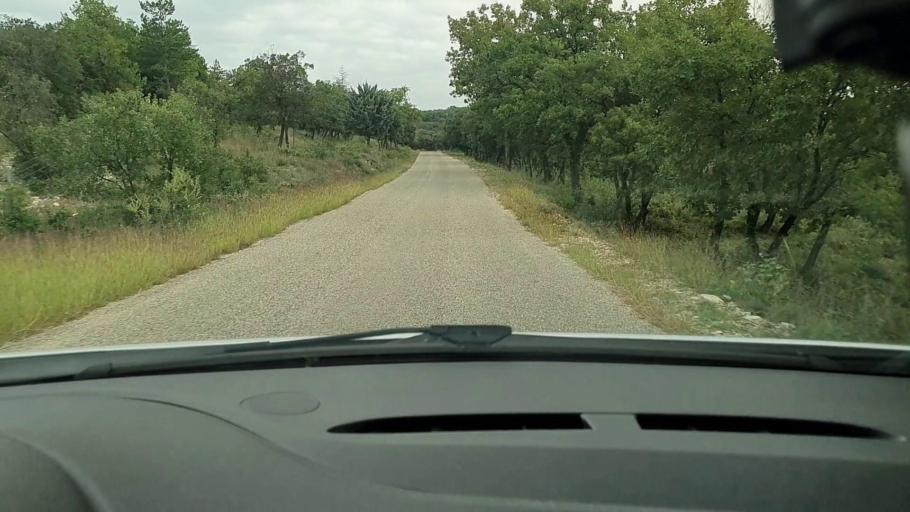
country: FR
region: Languedoc-Roussillon
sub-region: Departement du Gard
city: Montaren-et-Saint-Mediers
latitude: 44.1018
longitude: 4.3004
